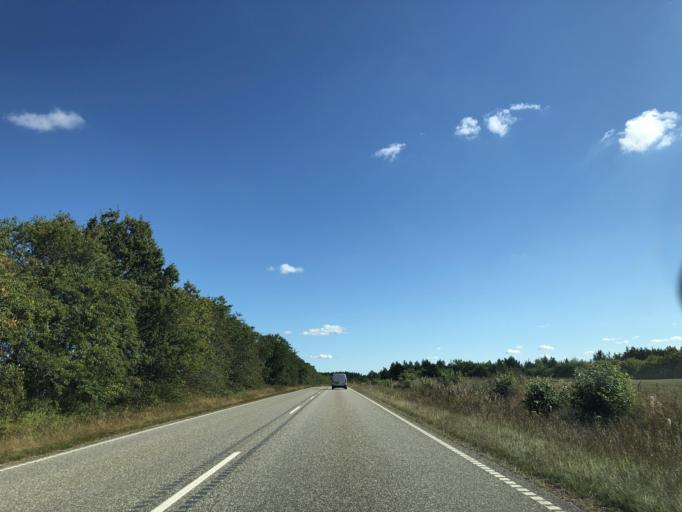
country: DK
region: Central Jutland
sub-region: Viborg Kommune
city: Karup
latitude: 56.3385
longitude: 9.0553
